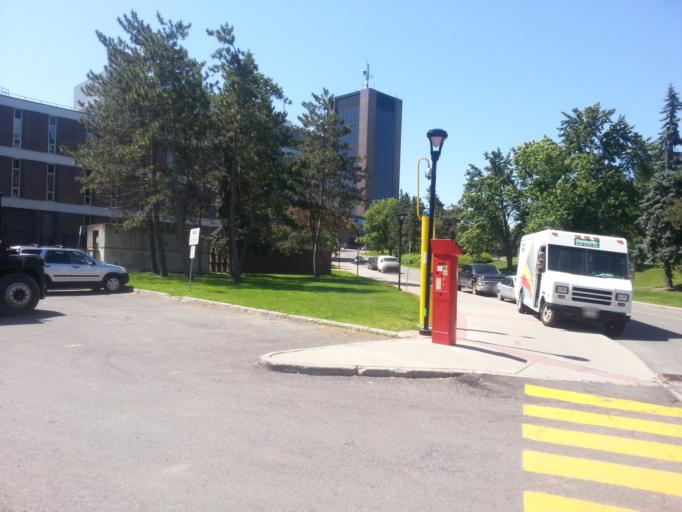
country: CA
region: Ontario
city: Ottawa
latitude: 45.3853
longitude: -75.6986
